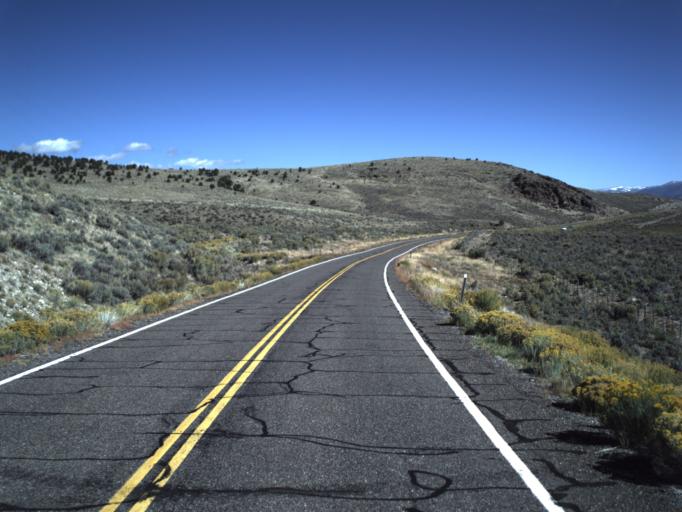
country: US
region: Utah
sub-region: Piute County
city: Junction
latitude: 38.3465
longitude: -111.9520
